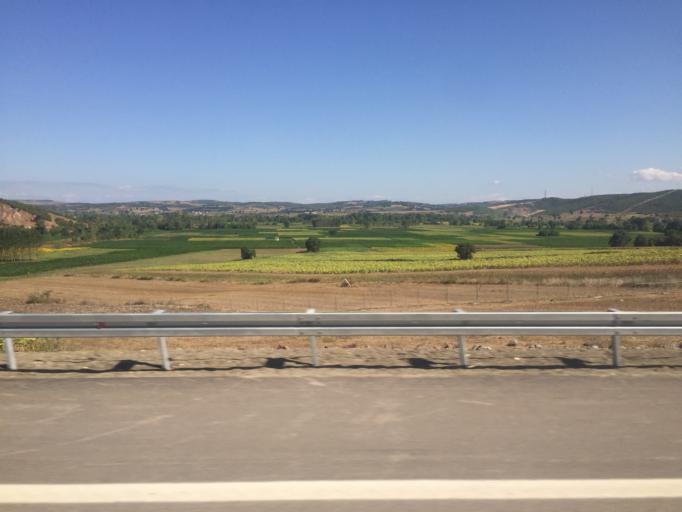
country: TR
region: Bursa
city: Mahmudiye
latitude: 40.2651
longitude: 28.6572
